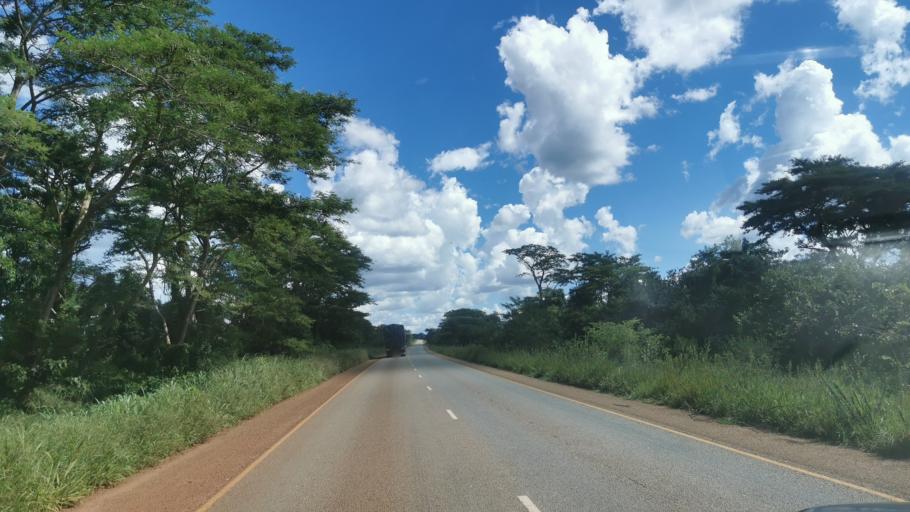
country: TZ
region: Geita
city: Uyovu
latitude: -3.0525
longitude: 31.2562
